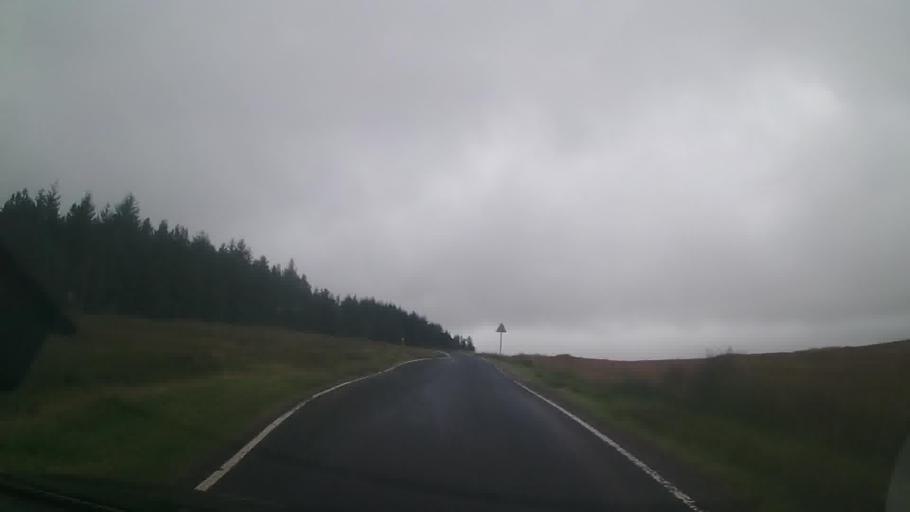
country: GB
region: Scotland
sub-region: Argyll and Bute
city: Isle Of Mull
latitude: 56.7242
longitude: -6.0464
